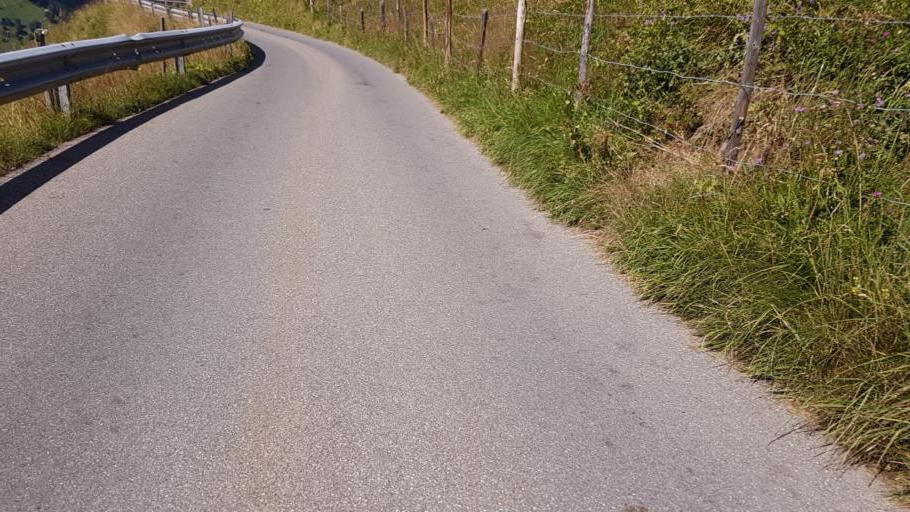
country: CH
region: Bern
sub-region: Frutigen-Niedersimmental District
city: Adelboden
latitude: 46.5218
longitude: 7.6081
